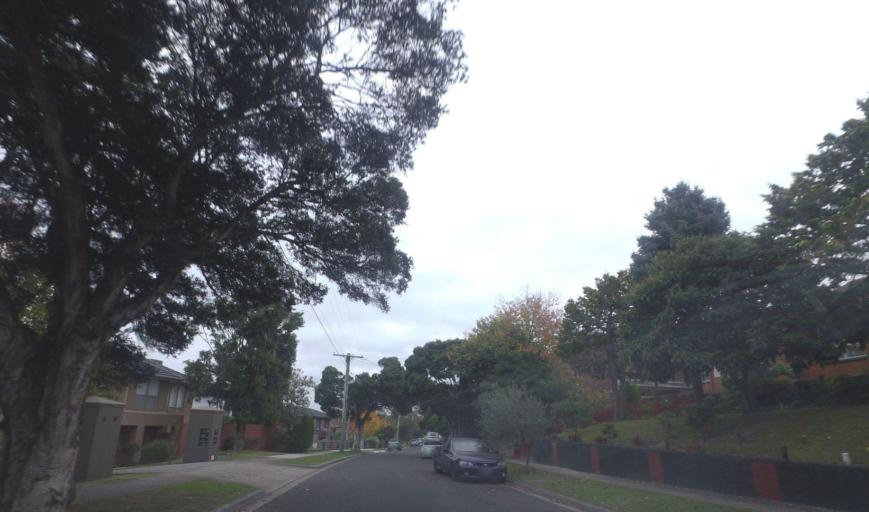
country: AU
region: Victoria
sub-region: Manningham
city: Doncaster
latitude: -37.7956
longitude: 145.1217
